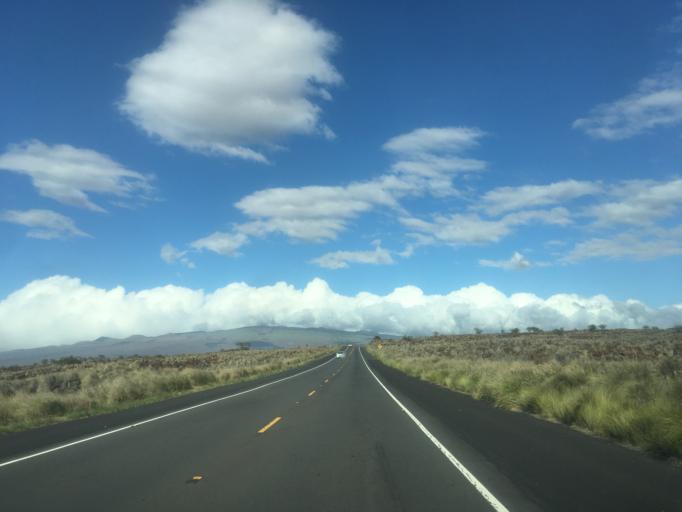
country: US
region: Hawaii
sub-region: Hawaii County
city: Waikoloa Village
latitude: 19.9166
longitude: -155.8062
